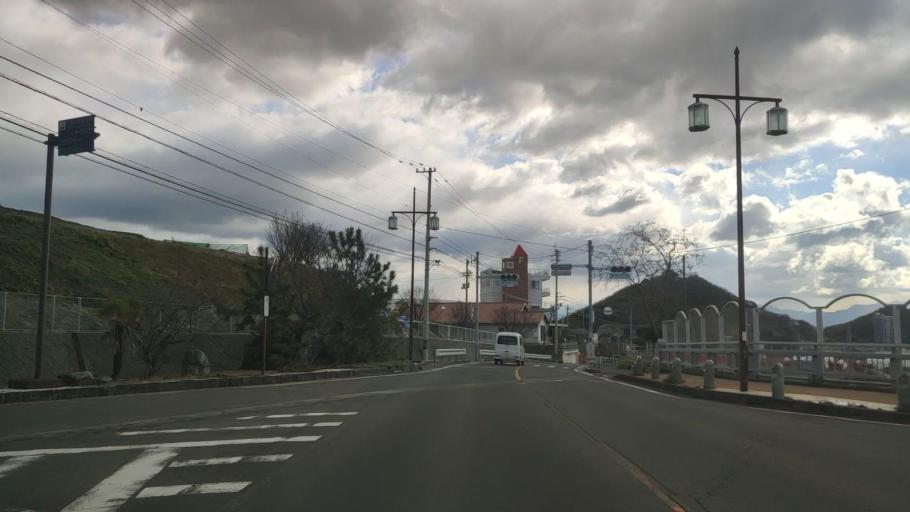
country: JP
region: Ehime
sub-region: Shikoku-chuo Shi
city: Matsuyama
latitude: 33.8777
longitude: 132.7042
